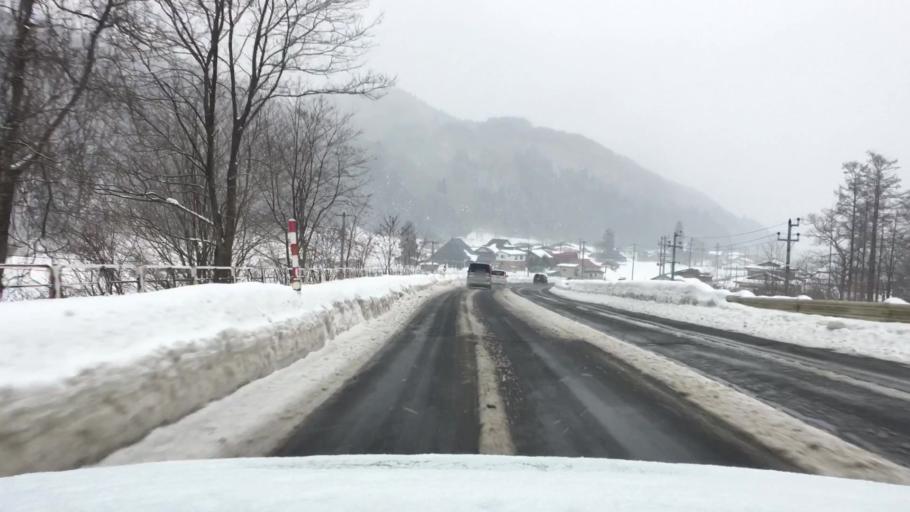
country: JP
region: Akita
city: Hanawa
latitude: 40.0641
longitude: 141.0154
